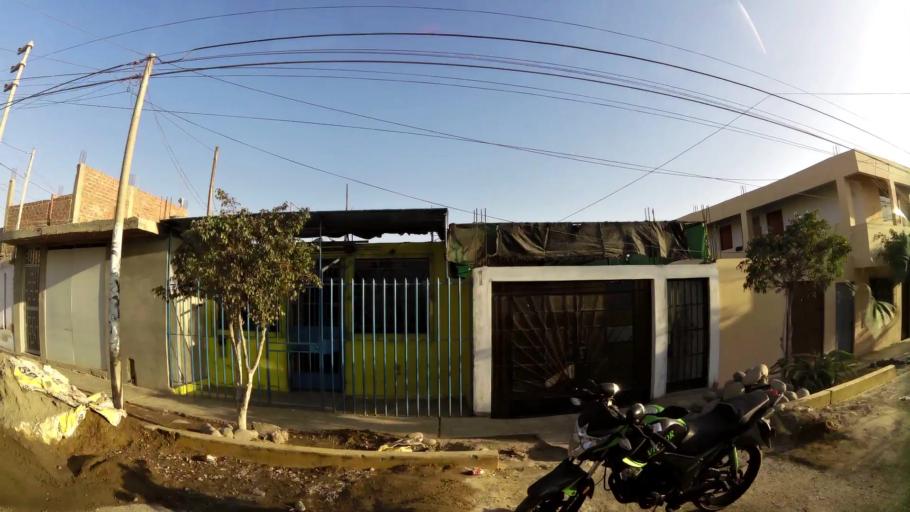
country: PE
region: Ica
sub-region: Provincia de Pisco
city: Villa Tupac Amaru
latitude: -13.7158
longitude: -76.1505
